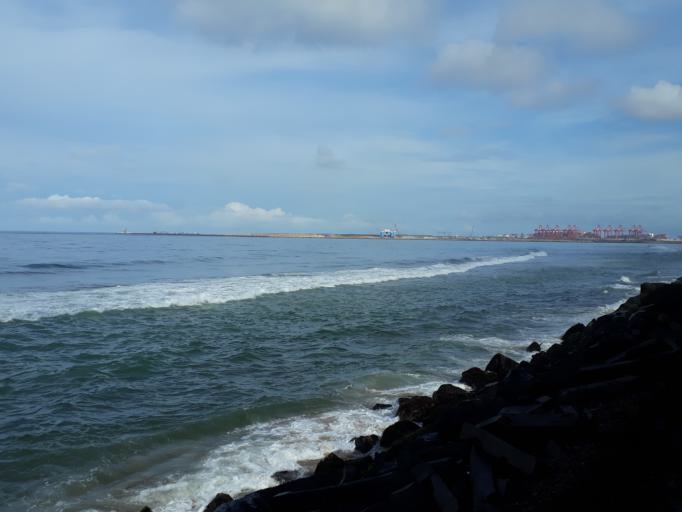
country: LK
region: Western
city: Colombo
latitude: 6.9122
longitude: 79.8479
